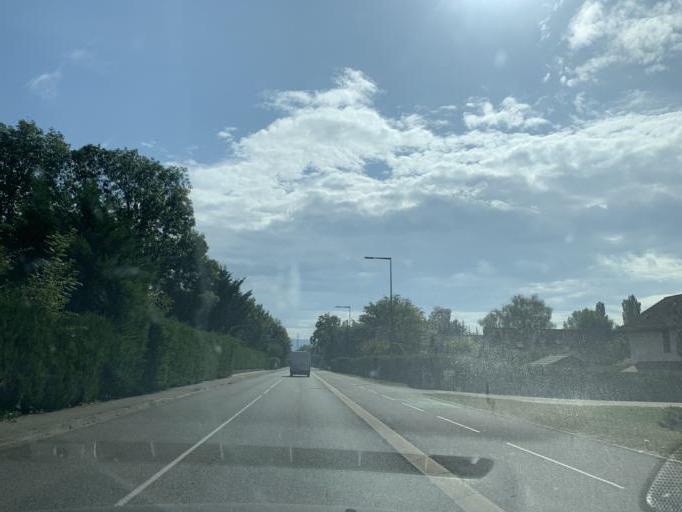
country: FR
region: Rhone-Alpes
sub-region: Departement de l'Ain
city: Divonne-les-Bains
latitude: 46.3471
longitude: 6.1389
